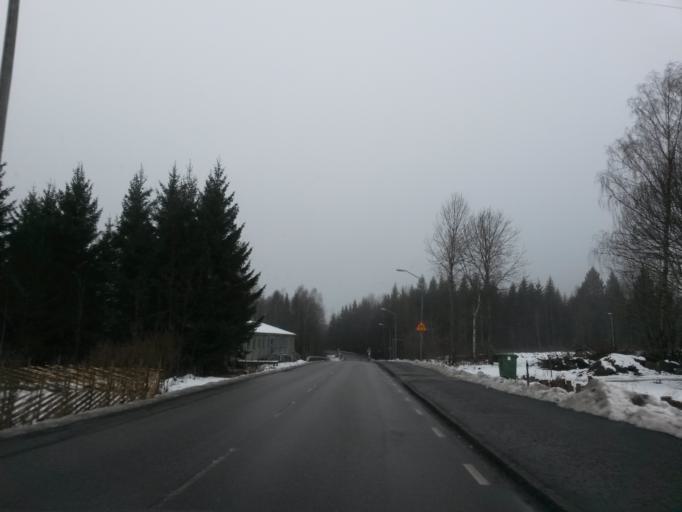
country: SE
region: Vaestra Goetaland
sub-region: Ulricehamns Kommun
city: Ulricehamn
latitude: 57.6665
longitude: 13.4202
